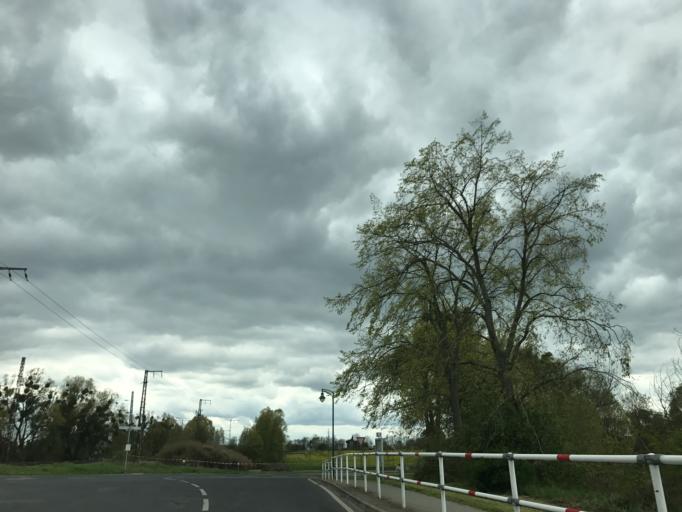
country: DE
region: Brandenburg
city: Wustermark
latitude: 52.5155
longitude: 12.9708
